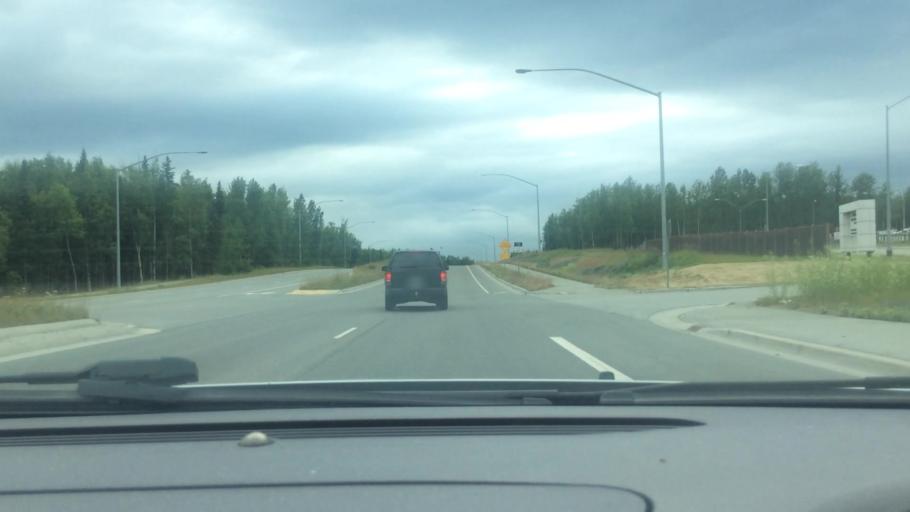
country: US
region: Alaska
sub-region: Anchorage Municipality
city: Anchorage
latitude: 61.1789
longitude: -149.7812
